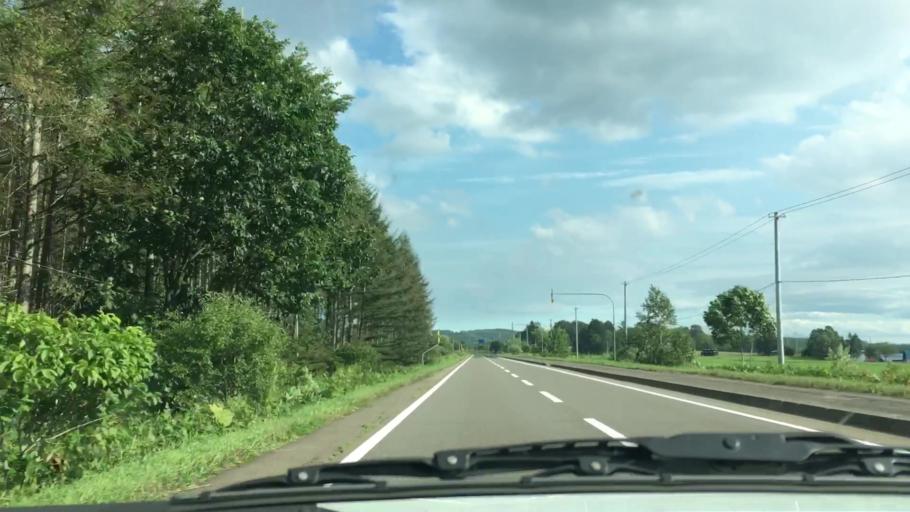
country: JP
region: Hokkaido
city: Otofuke
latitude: 43.3276
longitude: 143.2967
